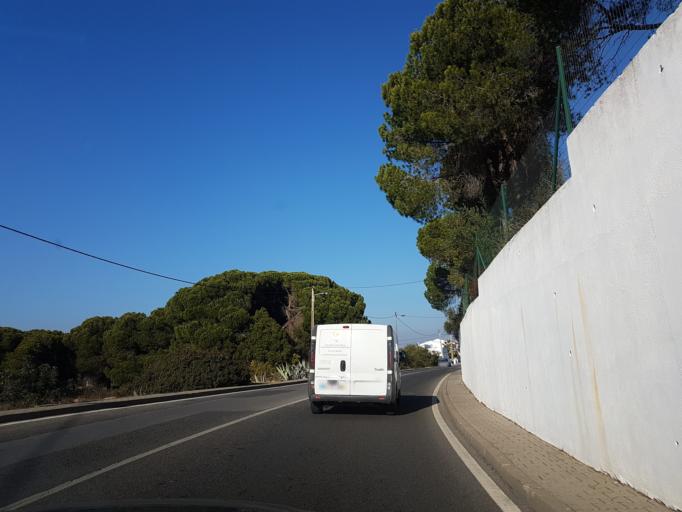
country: PT
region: Faro
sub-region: Albufeira
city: Ferreiras
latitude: 37.1049
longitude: -8.2147
